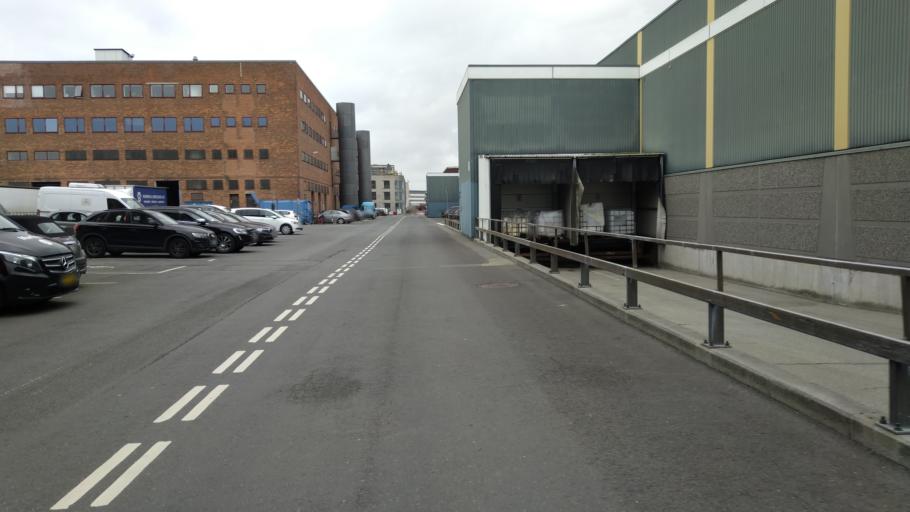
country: DK
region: Capital Region
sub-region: Kobenhavn
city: Christianshavn
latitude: 55.7093
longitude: 12.6026
